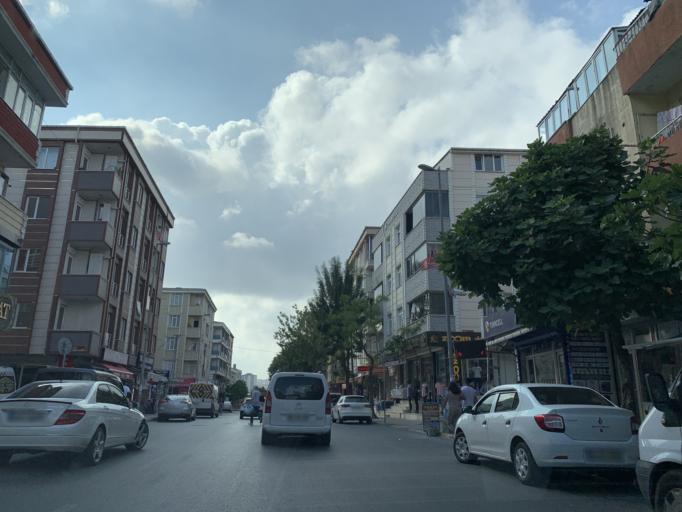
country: TR
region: Istanbul
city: Esenyurt
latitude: 41.0240
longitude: 28.6711
